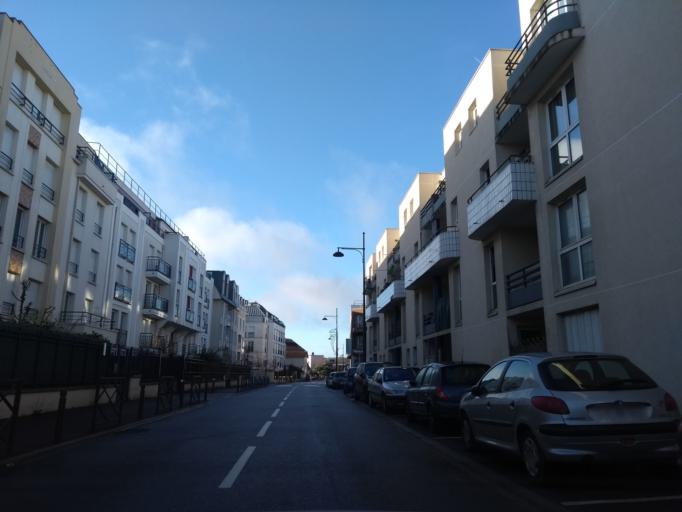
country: FR
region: Ile-de-France
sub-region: Departement des Hauts-de-Seine
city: Chatenay-Malabry
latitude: 48.7729
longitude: 2.2561
